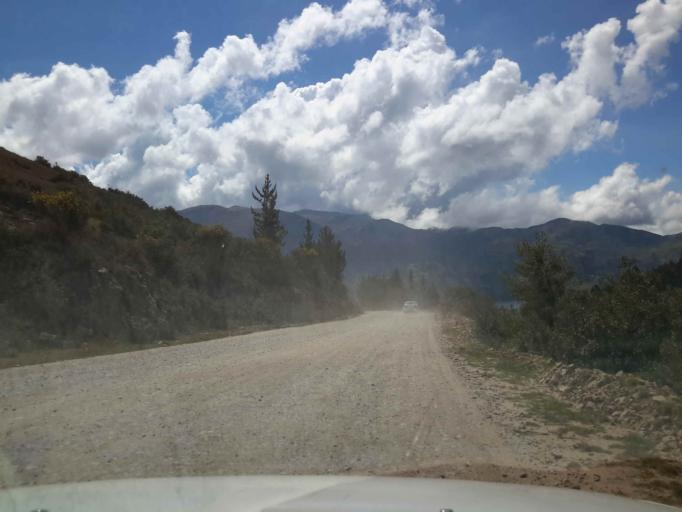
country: PE
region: Apurimac
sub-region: Provincia de Andahuaylas
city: Pacucha
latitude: -13.6288
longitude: -73.3387
